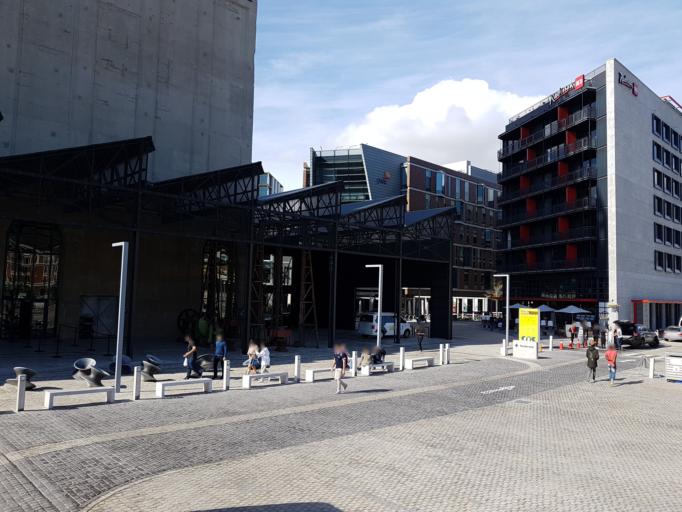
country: ZA
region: Western Cape
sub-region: City of Cape Town
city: Cape Town
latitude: -33.9084
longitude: 18.4223
